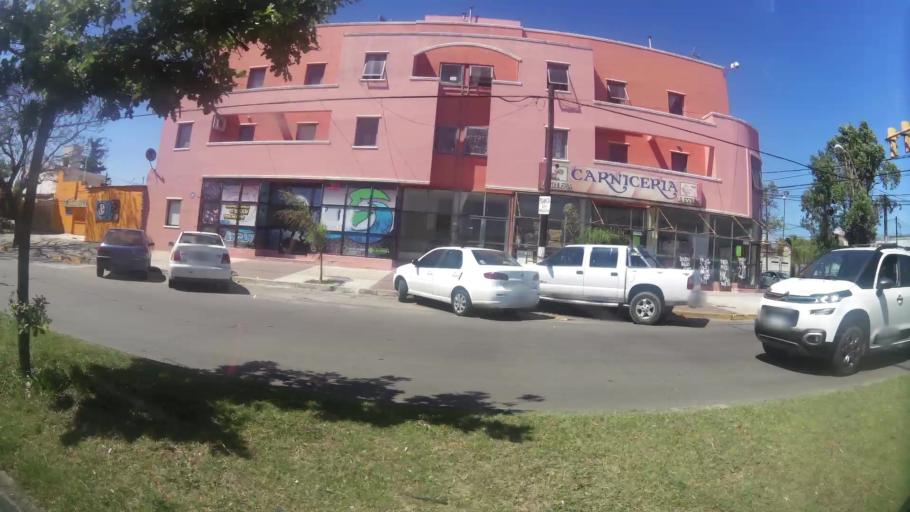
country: AR
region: Cordoba
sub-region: Departamento de Capital
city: Cordoba
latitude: -31.4199
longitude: -64.2164
